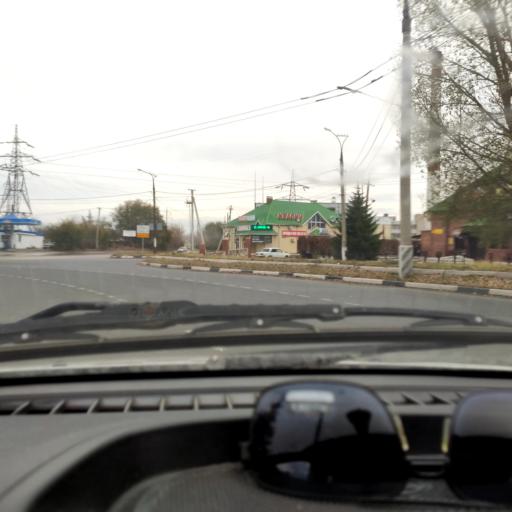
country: RU
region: Samara
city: Zhigulevsk
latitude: 53.5103
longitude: 49.4628
